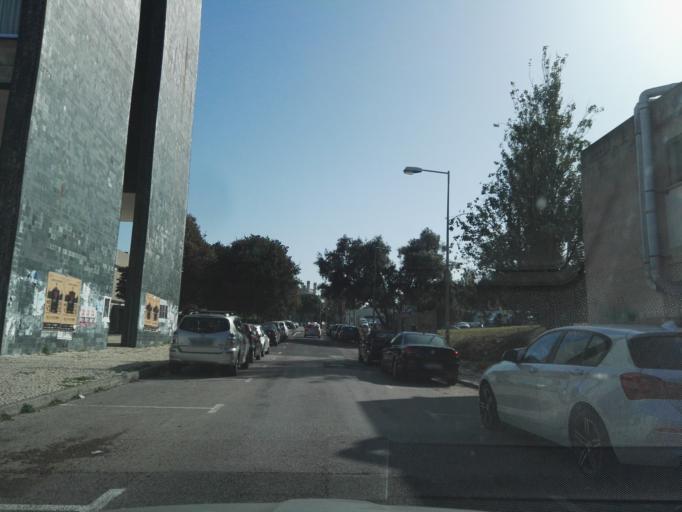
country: PT
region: Lisbon
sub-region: Lisbon
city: Lisbon
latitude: 38.7498
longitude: -9.1559
